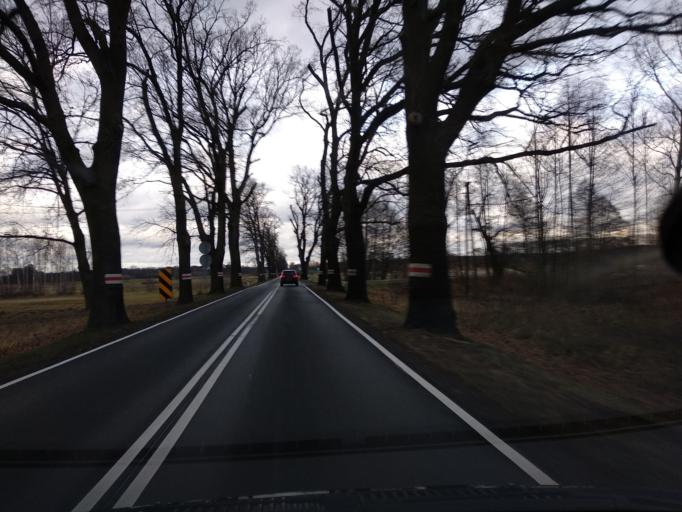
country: PL
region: Lower Silesian Voivodeship
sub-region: Powiat olesnicki
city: Miedzyborz
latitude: 51.4776
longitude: 17.7521
